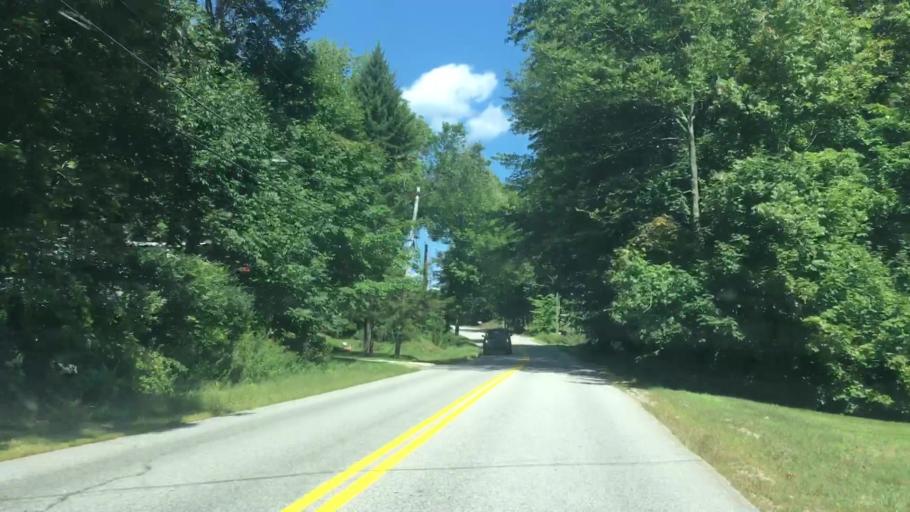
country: US
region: Maine
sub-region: Cumberland County
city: New Gloucester
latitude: 43.9405
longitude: -70.3019
